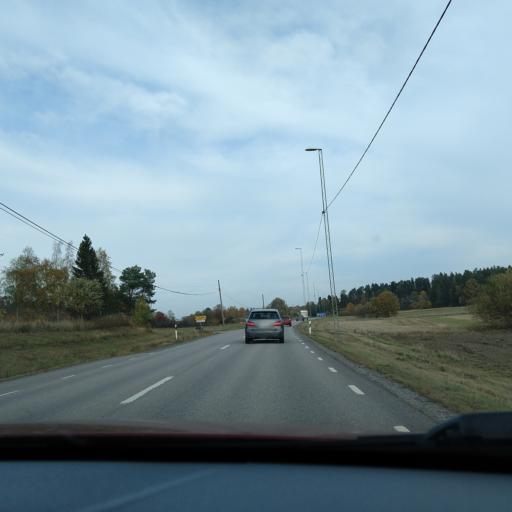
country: SE
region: Stockholm
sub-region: Upplands Vasby Kommun
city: Upplands Vaesby
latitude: 59.5327
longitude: 17.9905
